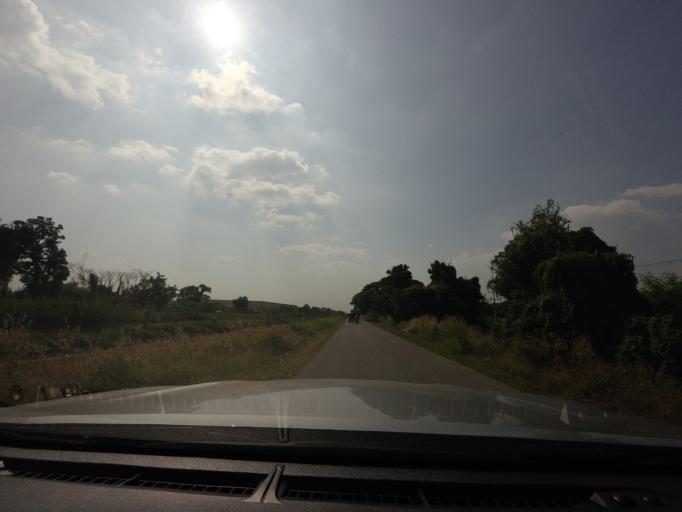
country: TH
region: Phitsanulok
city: Phitsanulok
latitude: 16.8148
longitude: 100.2302
